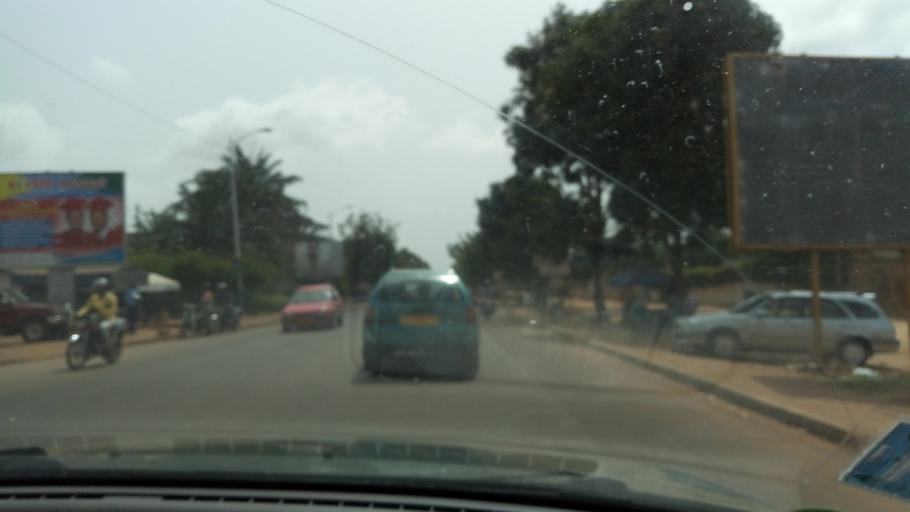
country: TG
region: Maritime
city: Lome
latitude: 6.1754
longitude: 1.1817
